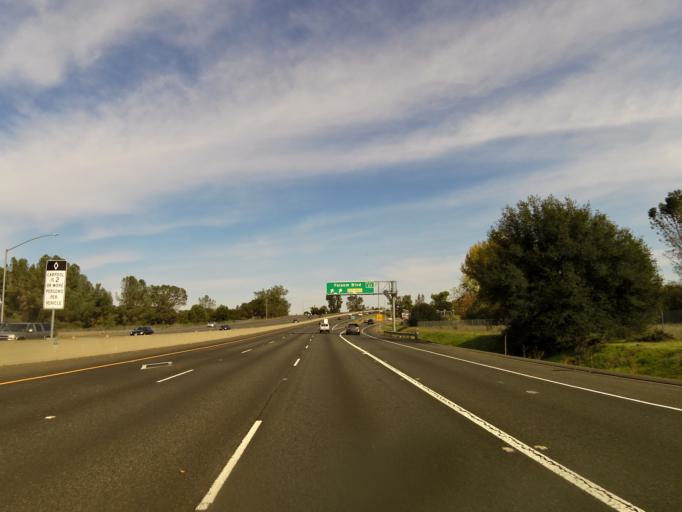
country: US
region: California
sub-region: Sacramento County
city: Gold River
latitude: 38.6377
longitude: -121.2039
